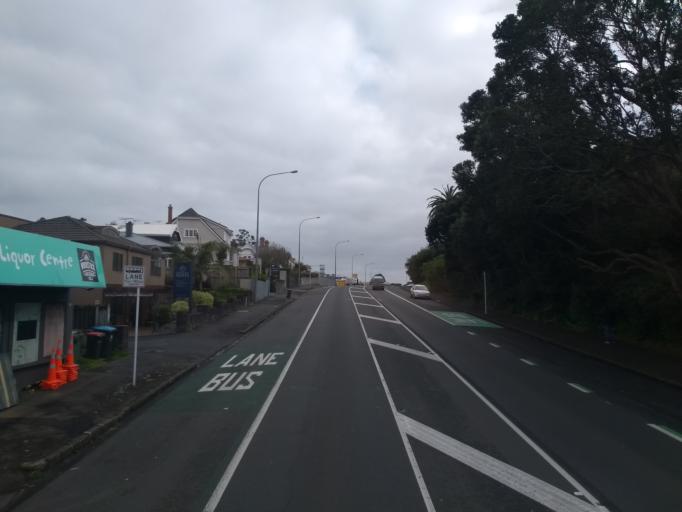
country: NZ
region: Auckland
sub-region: Auckland
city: Auckland
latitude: -36.8875
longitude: 174.7899
